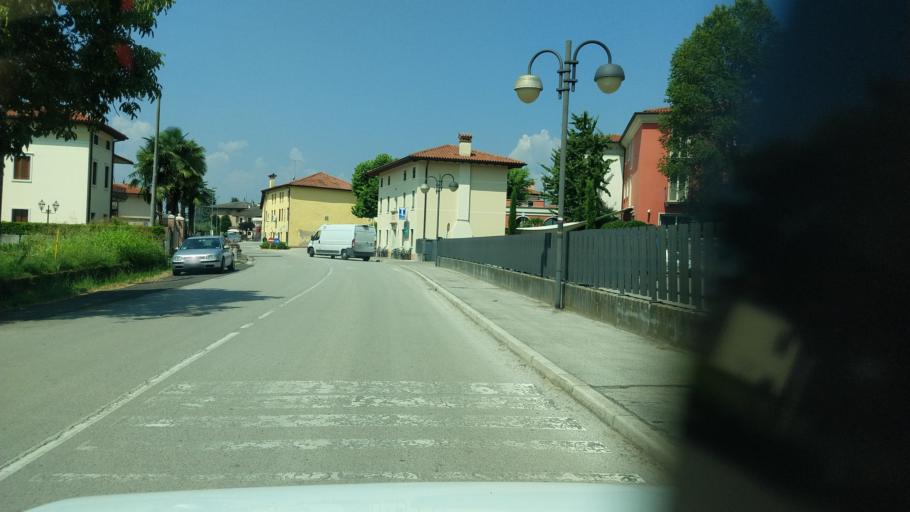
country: IT
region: Veneto
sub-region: Provincia di Vicenza
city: Schiavon
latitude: 45.6807
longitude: 11.6402
